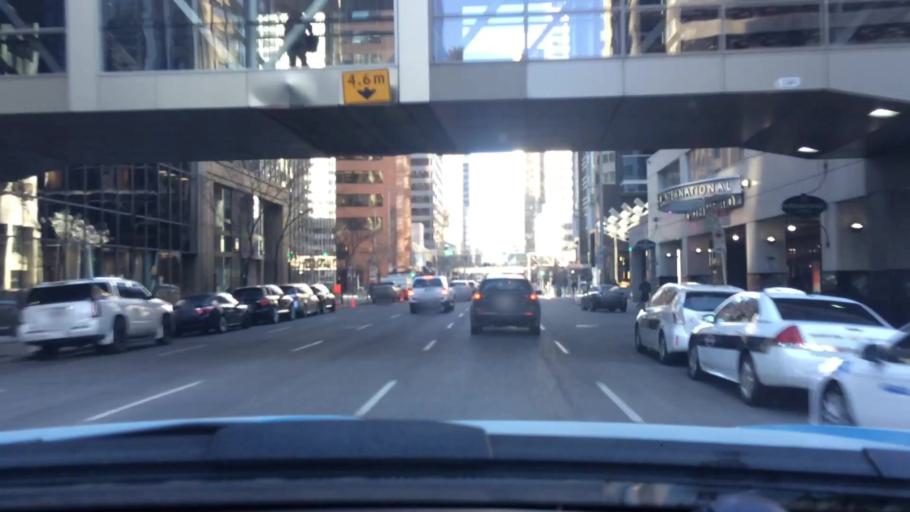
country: CA
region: Alberta
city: Calgary
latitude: 51.0495
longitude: -114.0661
